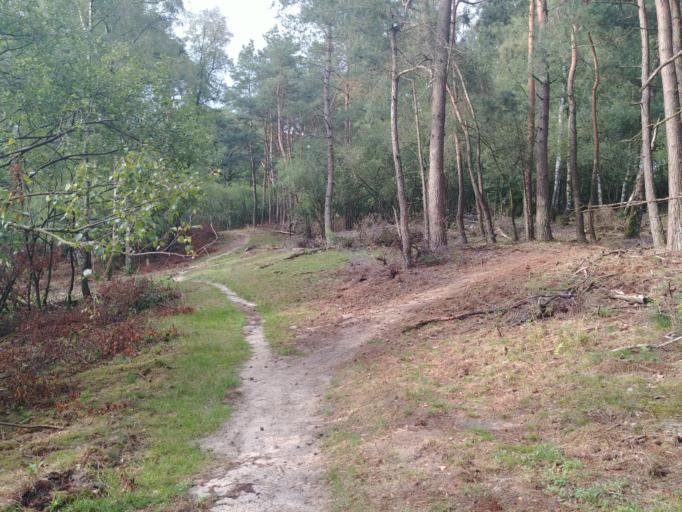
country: NL
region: Gelderland
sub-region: Gemeente Renkum
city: Wolfheze
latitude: 52.0432
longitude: 5.7700
